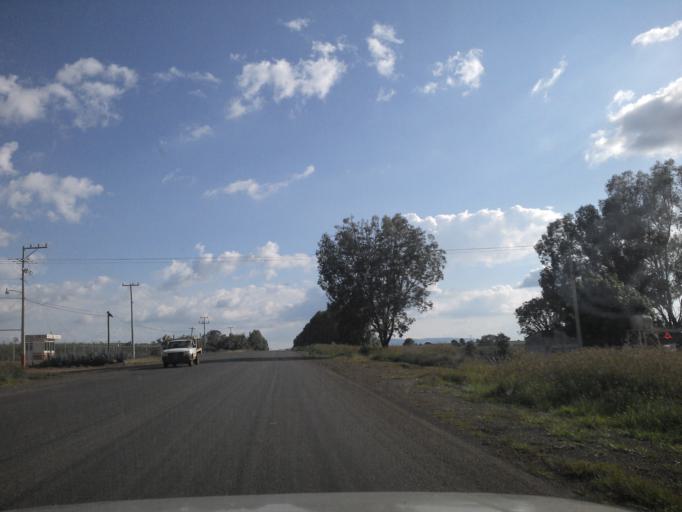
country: MX
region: Jalisco
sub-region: Atotonilco el Alto
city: Ojo de Agua de Moran
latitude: 20.5893
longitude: -102.4961
